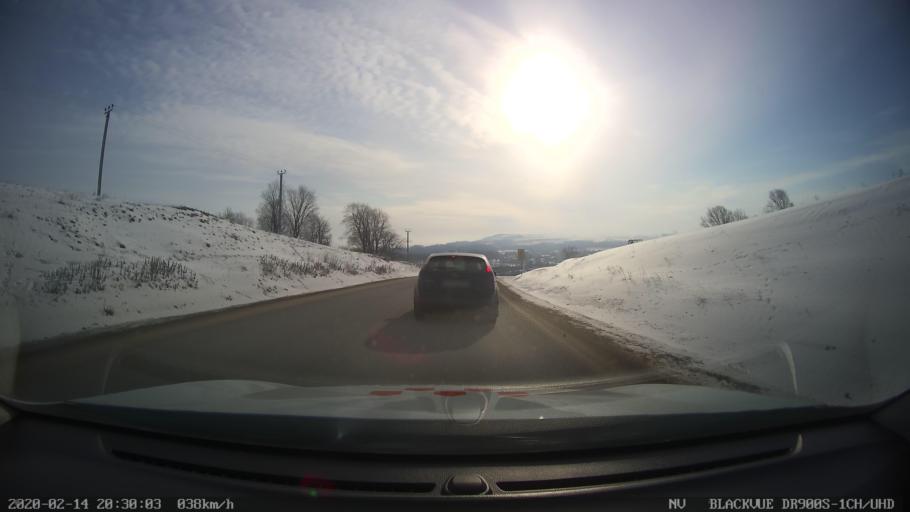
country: RU
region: Tatarstan
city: Stolbishchi
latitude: 55.4453
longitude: 48.9933
